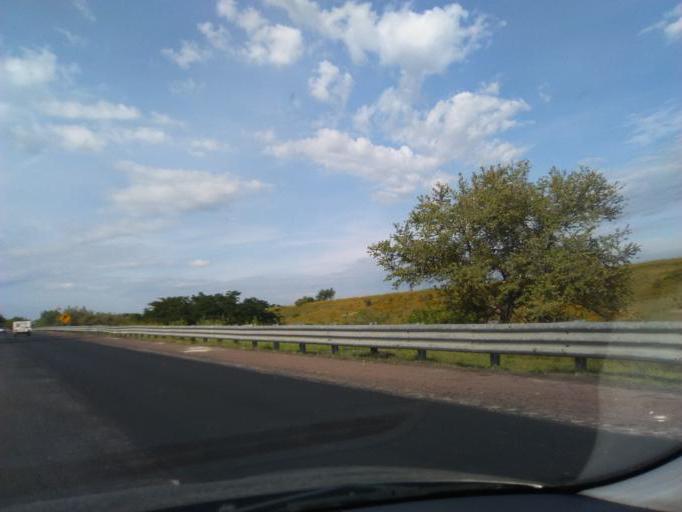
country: MX
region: Morelos
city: Ahuehuetzingo
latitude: 18.6702
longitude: -99.2949
